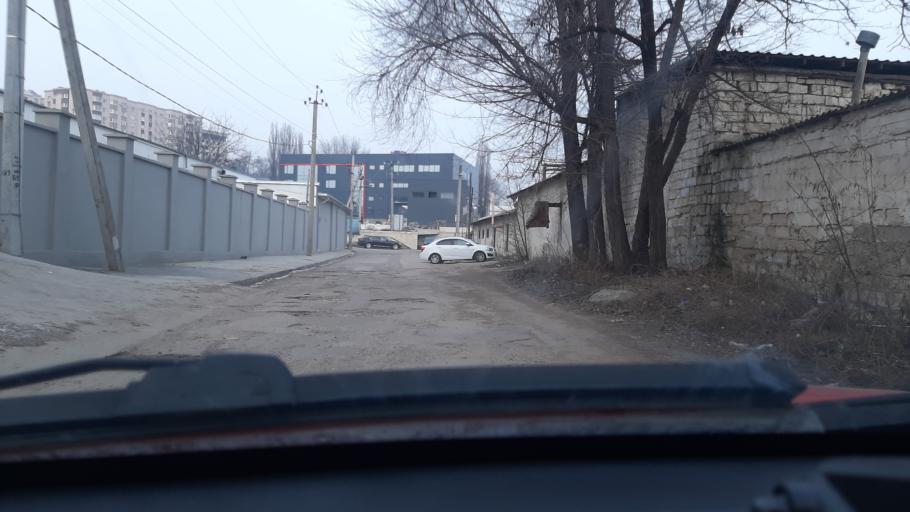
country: MD
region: Chisinau
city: Chisinau
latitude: 46.9901
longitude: 28.8862
